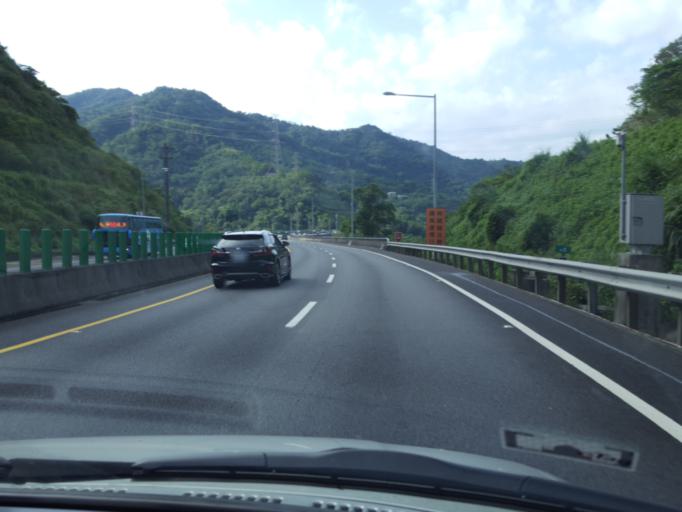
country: TW
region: Taipei
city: Taipei
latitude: 24.9895
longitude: 121.6580
